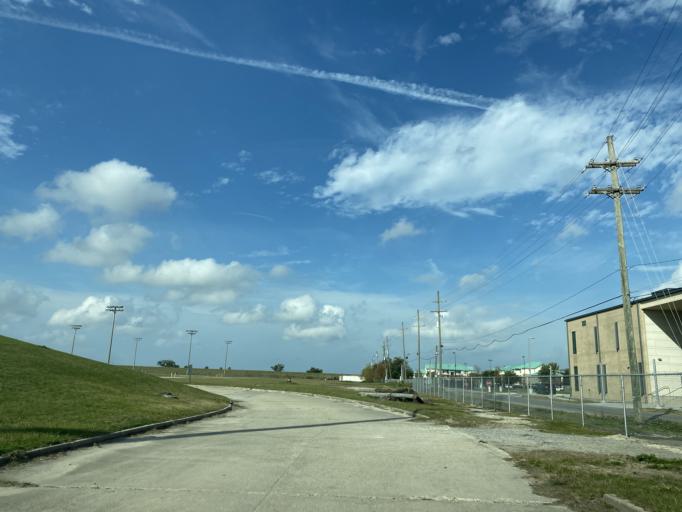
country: US
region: Louisiana
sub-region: Orleans Parish
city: New Orleans
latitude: 30.0309
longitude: -90.0463
